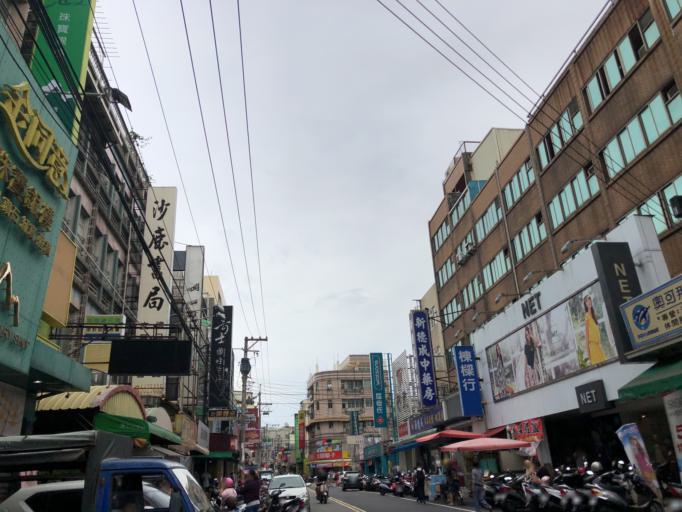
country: TW
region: Taiwan
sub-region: Taichung City
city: Taichung
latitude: 24.2367
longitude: 120.5586
